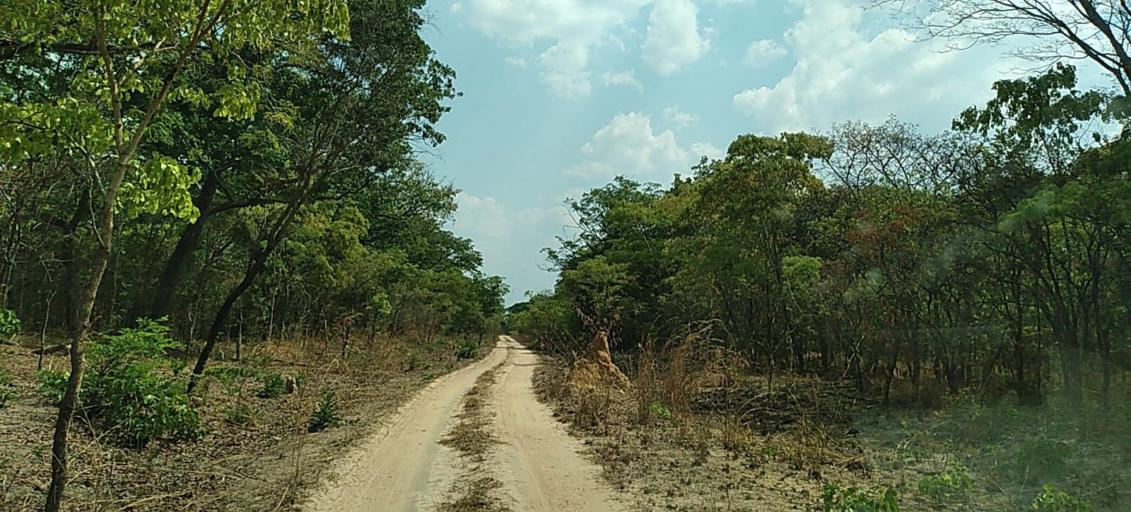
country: ZM
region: Copperbelt
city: Mpongwe
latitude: -13.8637
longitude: 27.9263
